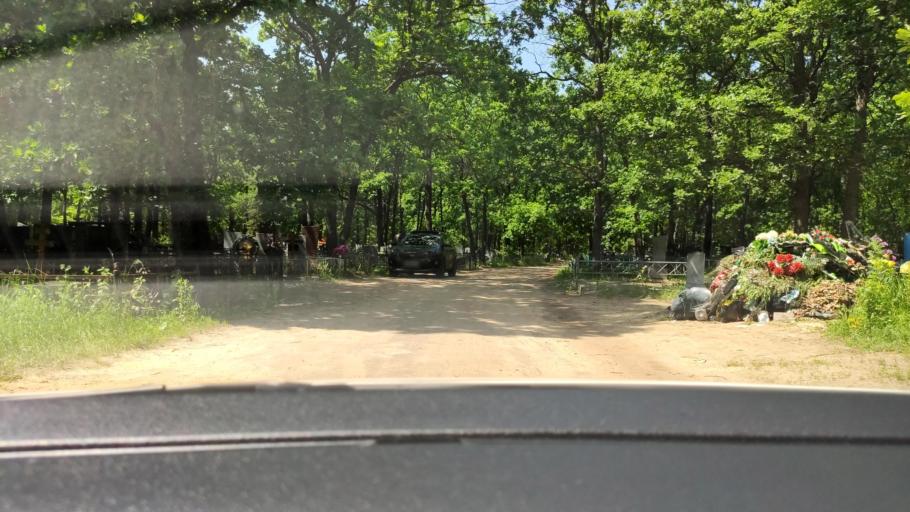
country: RU
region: Voronezj
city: Pridonskoy
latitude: 51.6680
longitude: 39.0935
